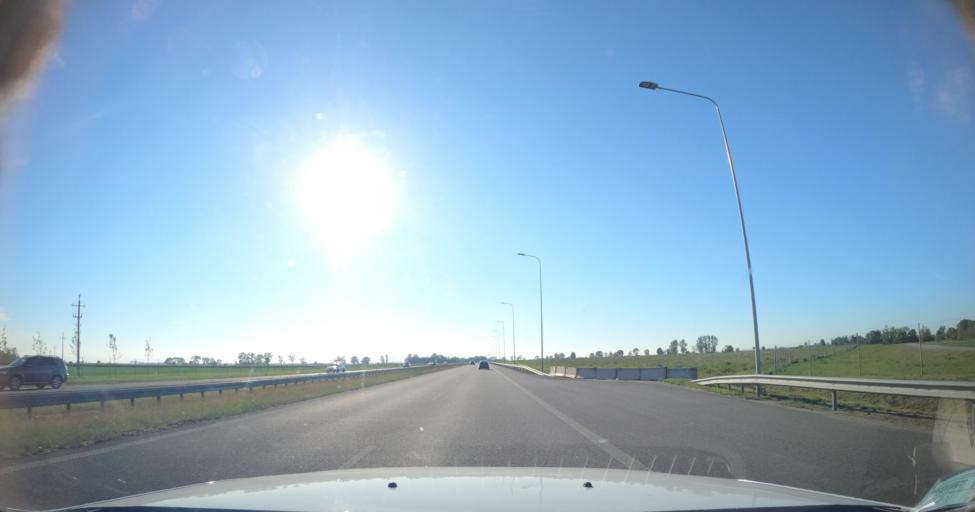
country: PL
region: Pomeranian Voivodeship
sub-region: Powiat nowodworski
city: Nowy Dwor Gdanski
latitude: 54.2212
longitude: 19.0703
